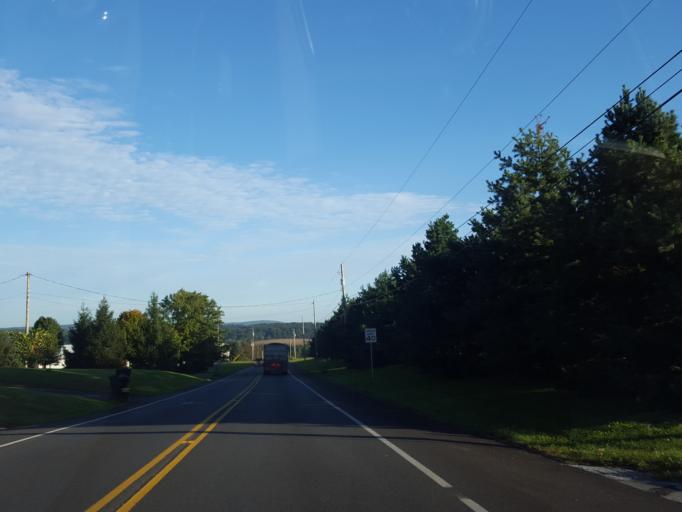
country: US
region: Pennsylvania
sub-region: York County
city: Windsor
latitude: 39.9482
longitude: -76.6053
